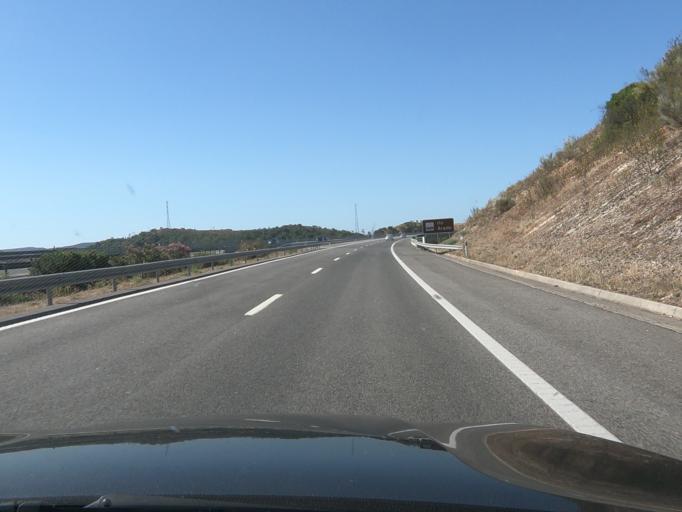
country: PT
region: Faro
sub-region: Silves
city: Sao Bartolomeu de Messines
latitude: 37.3096
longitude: -8.2540
